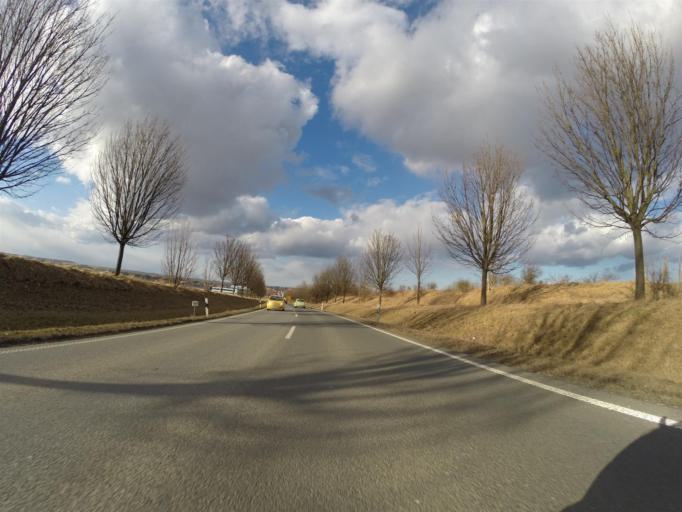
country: DE
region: Thuringia
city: Apolda
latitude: 51.0087
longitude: 11.5155
